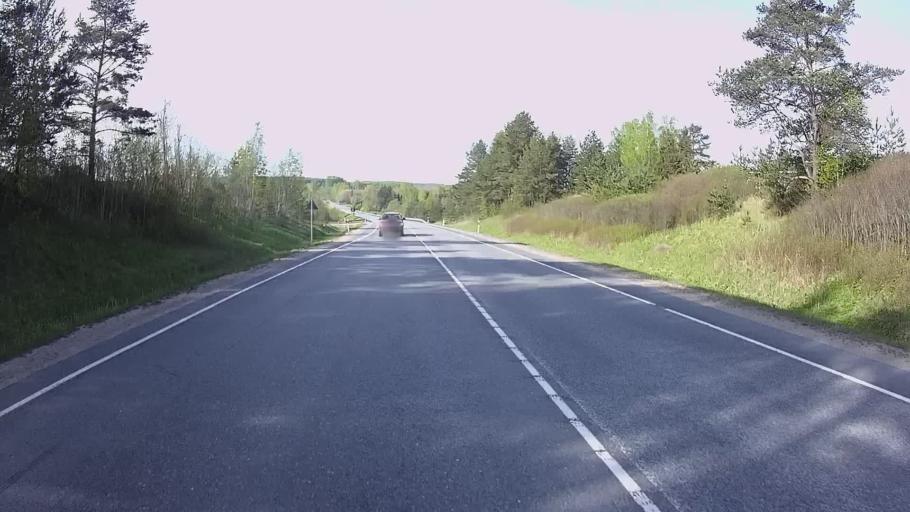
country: EE
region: Tartu
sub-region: UElenurme vald
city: Ulenurme
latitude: 58.2570
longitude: 26.6827
